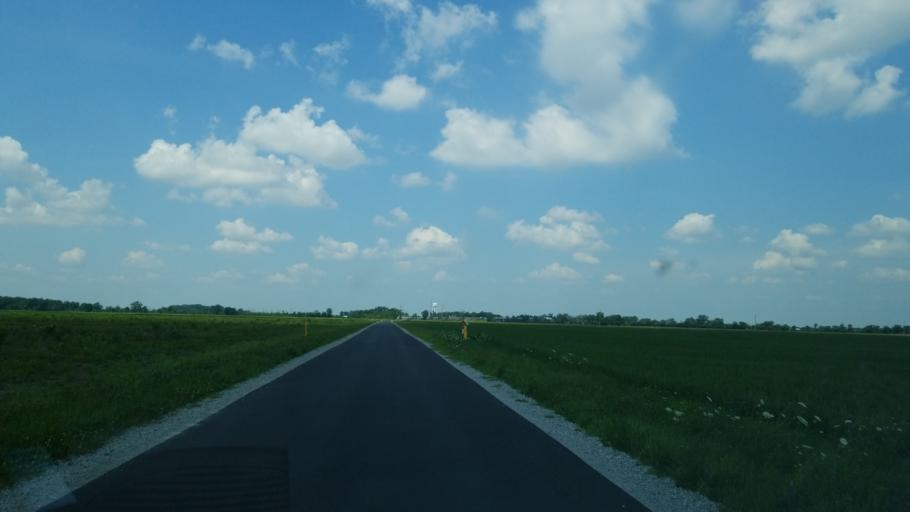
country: US
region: Ohio
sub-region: Wood County
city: North Baltimore
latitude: 41.2681
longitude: -83.6266
